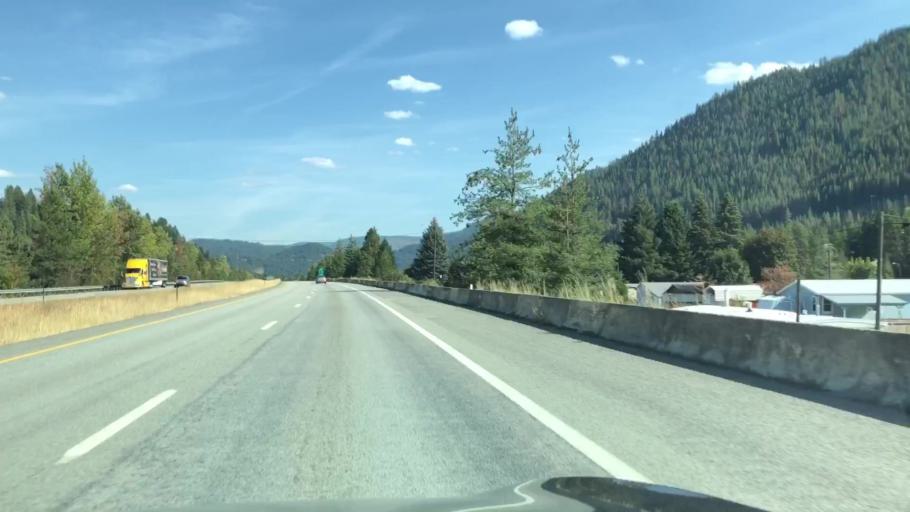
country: US
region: Idaho
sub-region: Shoshone County
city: Osburn
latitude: 47.5146
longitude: -116.0294
